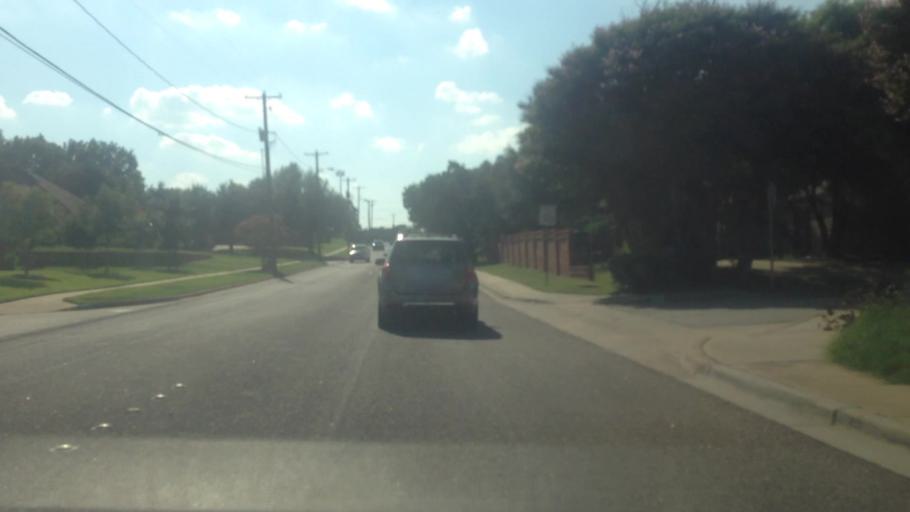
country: US
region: Texas
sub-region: Tarrant County
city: Colleyville
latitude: 32.8805
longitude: -97.1811
